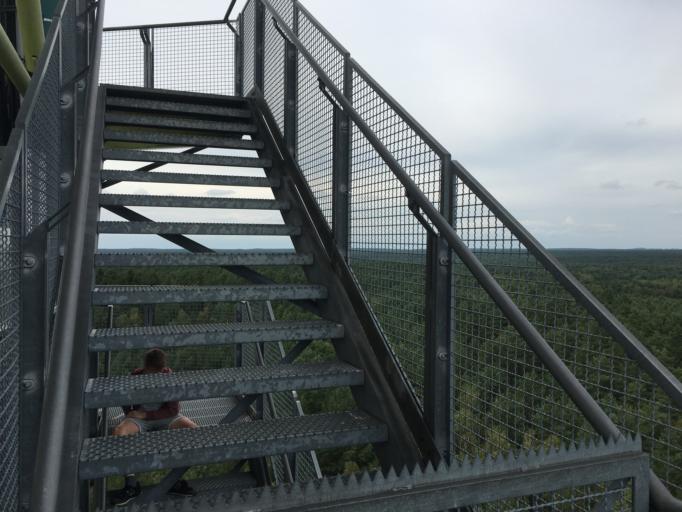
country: DE
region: Mecklenburg-Vorpommern
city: Mollenhagen
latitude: 53.4292
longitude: 12.8586
